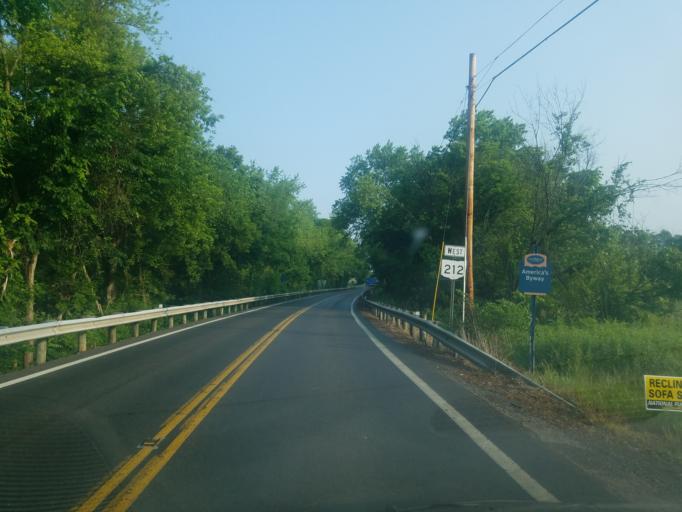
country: US
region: Ohio
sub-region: Tuscarawas County
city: Dover
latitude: 40.5800
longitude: -81.3933
